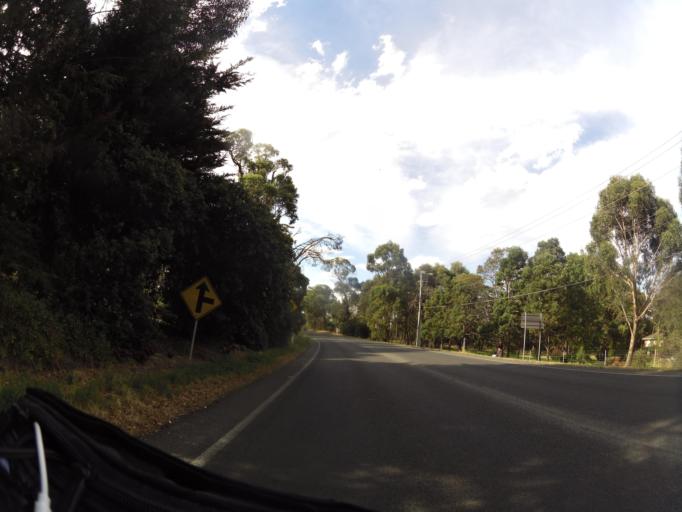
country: AU
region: Victoria
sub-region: Ballarat North
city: Mount Clear
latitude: -37.6298
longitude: 143.8807
